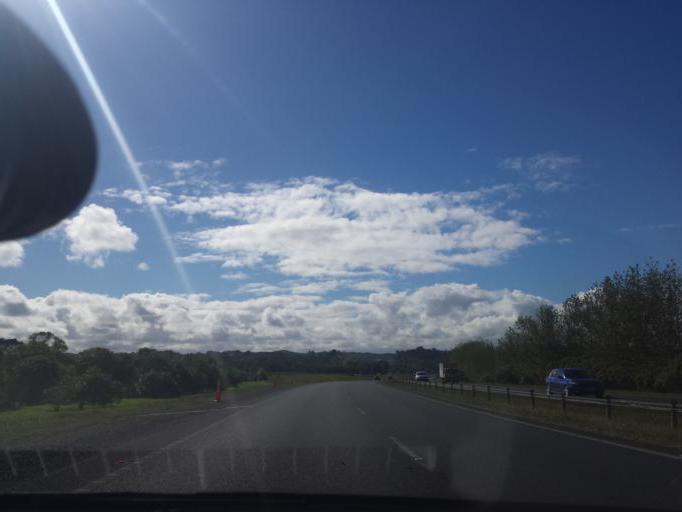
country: NZ
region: Auckland
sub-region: Auckland
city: Rothesay Bay
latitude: -36.6096
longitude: 174.6600
